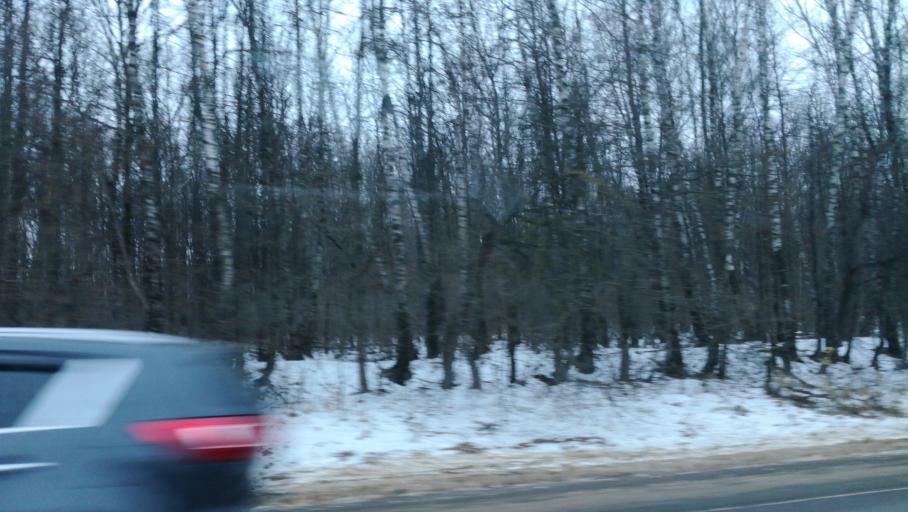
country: RU
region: Tula
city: Kosaya Gora
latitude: 54.1748
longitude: 37.4963
